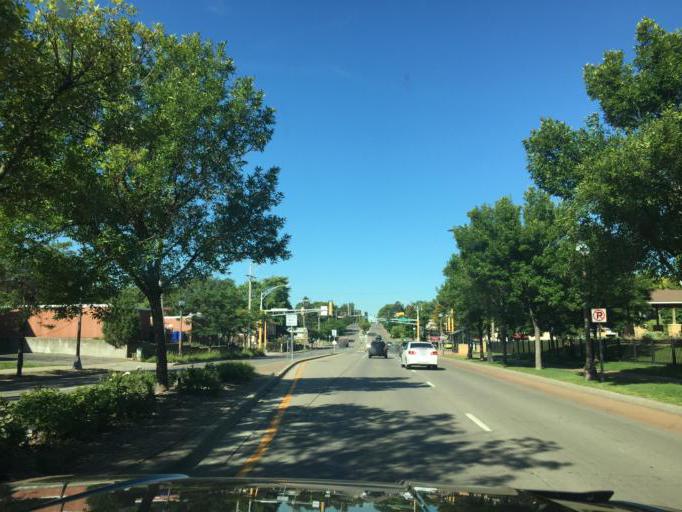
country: US
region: Minnesota
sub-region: Ramsey County
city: Roseville
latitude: 44.9920
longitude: -93.1503
